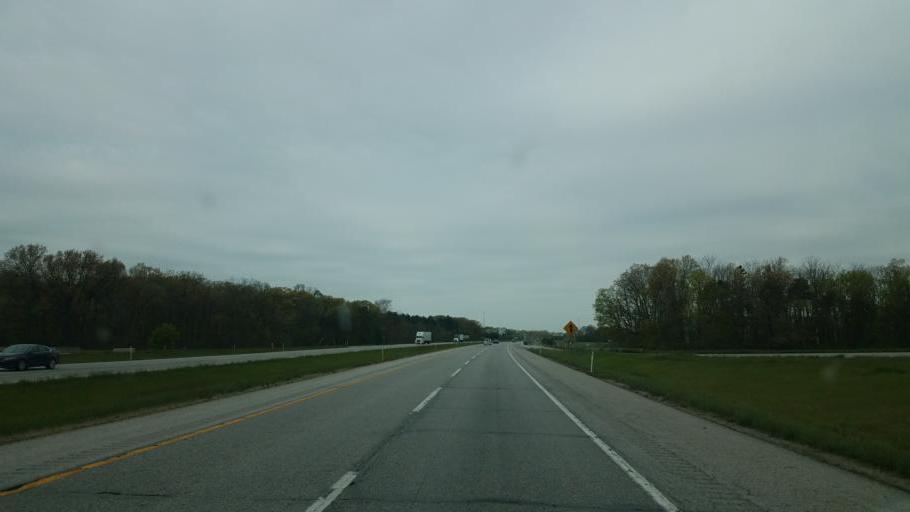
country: US
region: Michigan
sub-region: Saint Joseph County
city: White Pigeon
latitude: 41.7488
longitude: -85.6665
